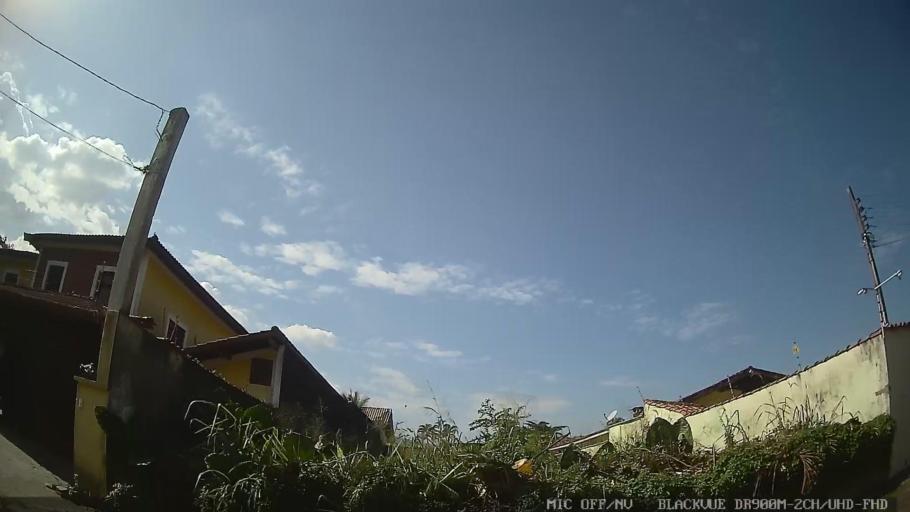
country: BR
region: Sao Paulo
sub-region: Guaruja
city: Guaruja
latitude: -23.9804
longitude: -46.2173
